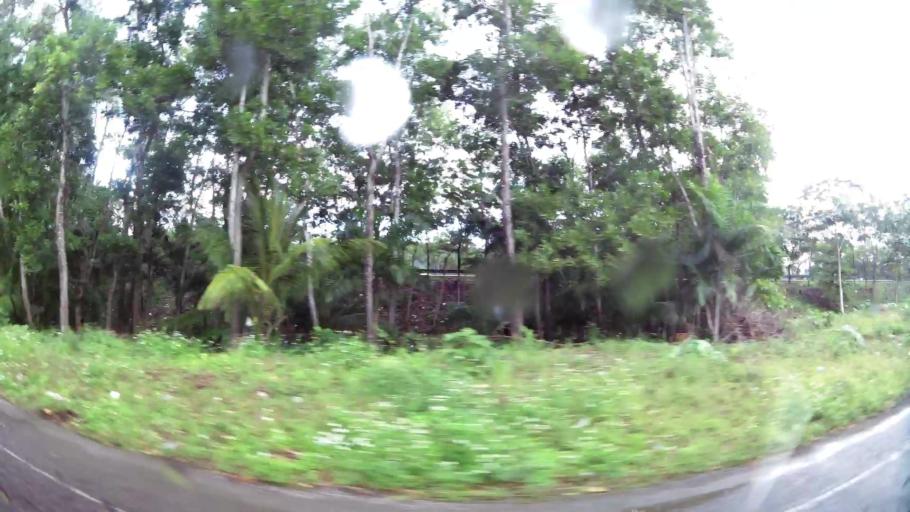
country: DO
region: Monsenor Nouel
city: Bonao
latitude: 18.9377
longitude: -70.3916
